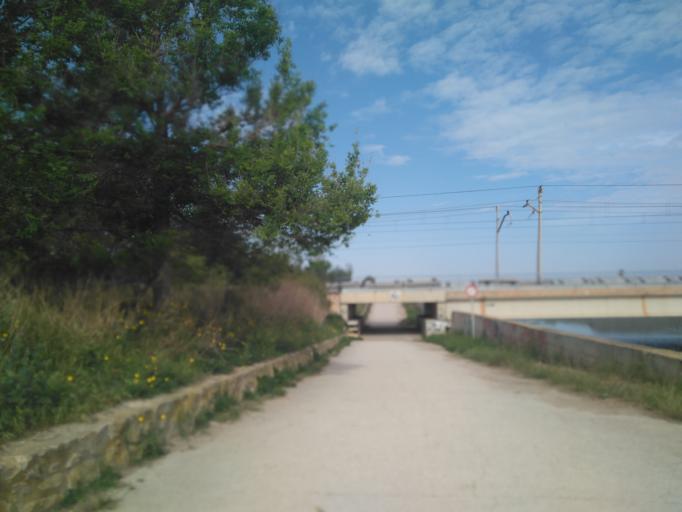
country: ES
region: Valencia
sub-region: Provincia de Valencia
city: Alboraya
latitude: 39.5018
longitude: -0.3279
